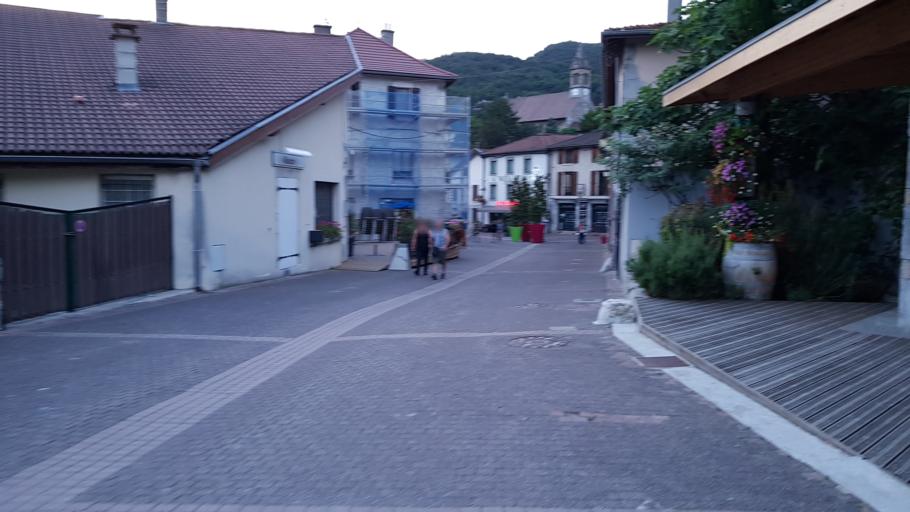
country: FR
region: Rhone-Alpes
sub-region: Departement de l'Isere
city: Fontanil-Cornillon
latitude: 45.2548
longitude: 5.6654
